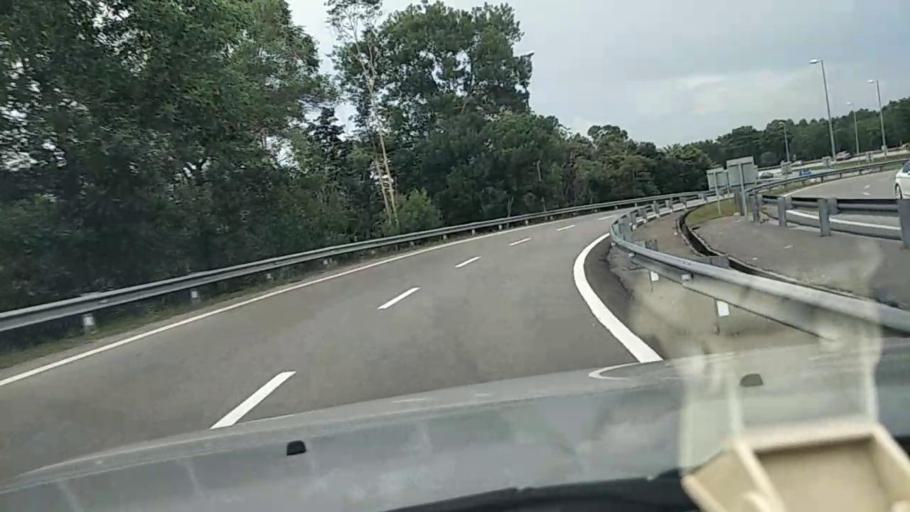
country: MY
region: Putrajaya
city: Putrajaya
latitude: 2.9228
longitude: 101.6023
